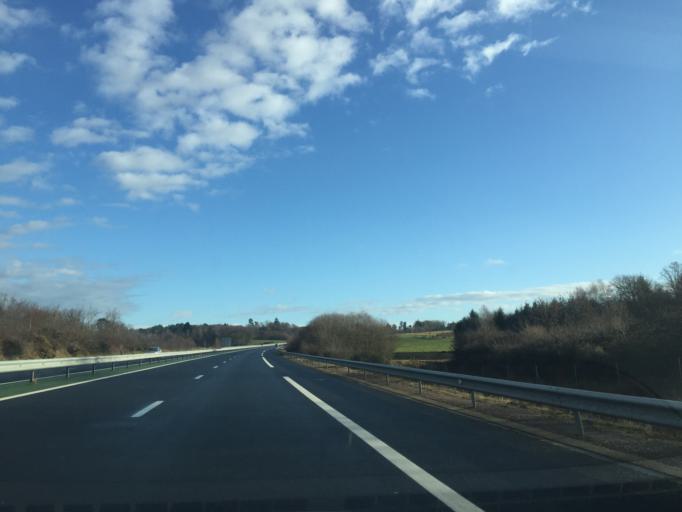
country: FR
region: Limousin
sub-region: Departement de la Correze
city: Saint-Mexant
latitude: 45.3041
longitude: 1.6573
